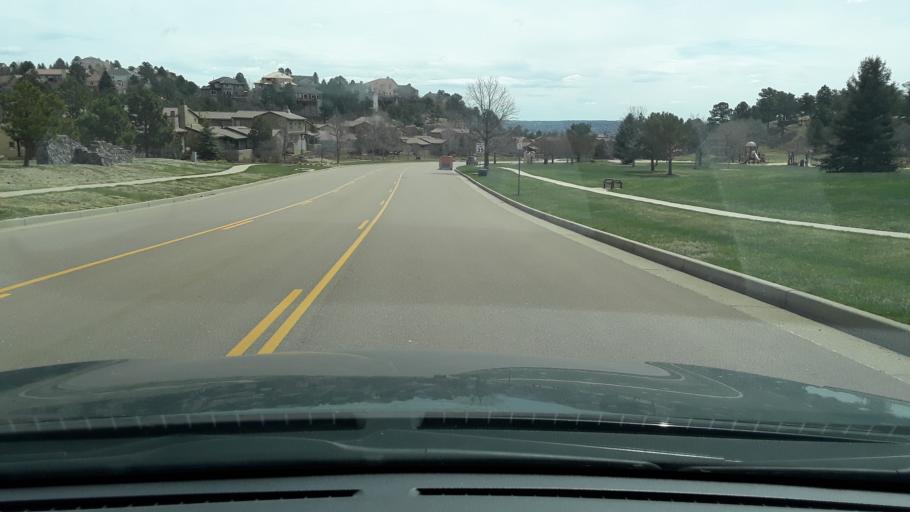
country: US
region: Colorado
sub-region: El Paso County
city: Air Force Academy
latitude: 38.9468
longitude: -104.8671
